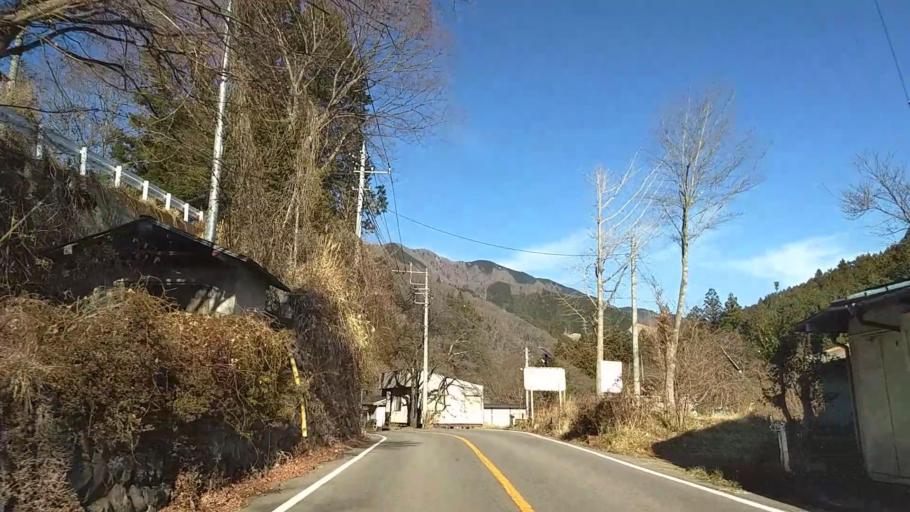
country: JP
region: Yamanashi
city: Otsuki
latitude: 35.5230
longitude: 139.0239
